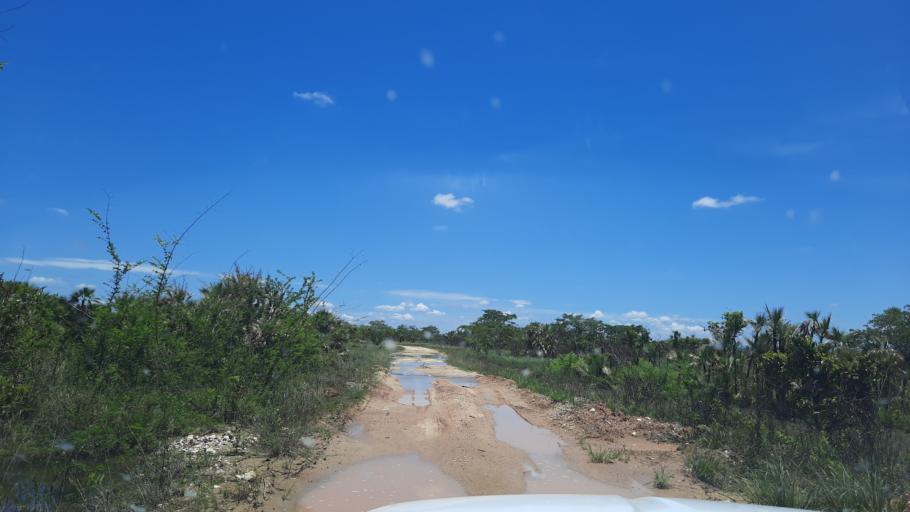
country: BZ
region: Cayo
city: Belmopan
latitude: 17.3837
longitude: -88.4940
